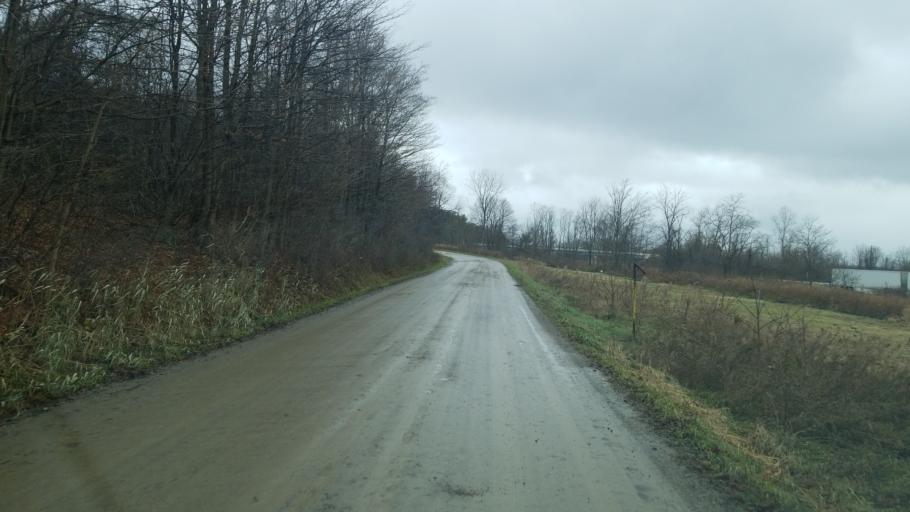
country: US
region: Ohio
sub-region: Ashtabula County
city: Conneaut
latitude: 41.9078
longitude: -80.5987
